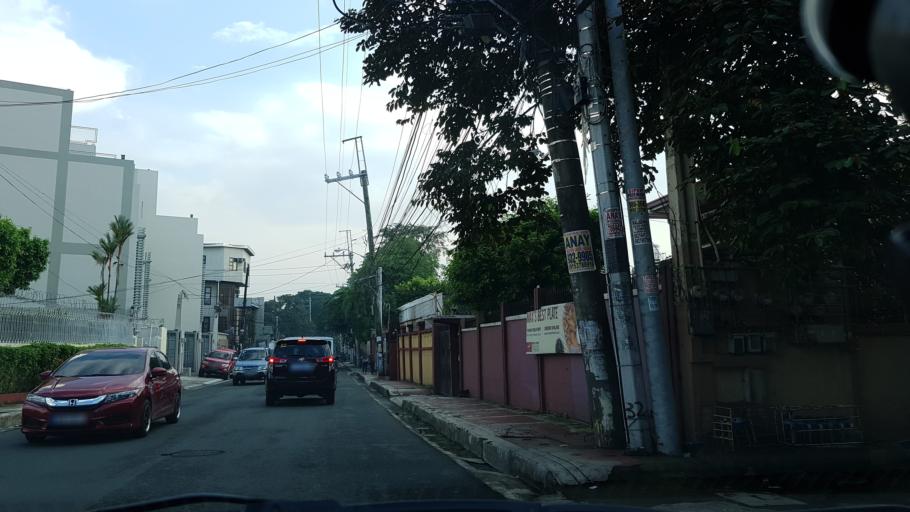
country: PH
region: Metro Manila
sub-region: Quezon City
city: Quezon City
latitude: 14.6386
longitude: 121.0581
